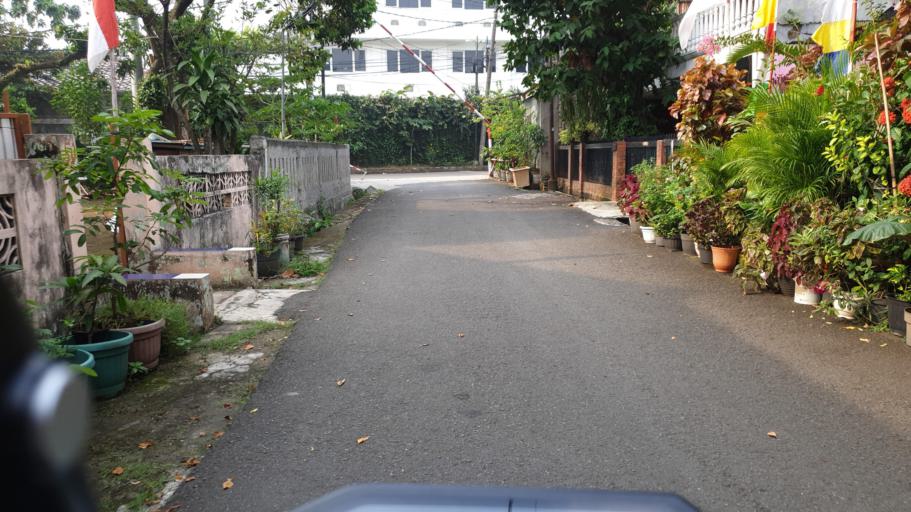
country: ID
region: West Java
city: Depok
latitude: -6.3393
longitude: 106.8312
